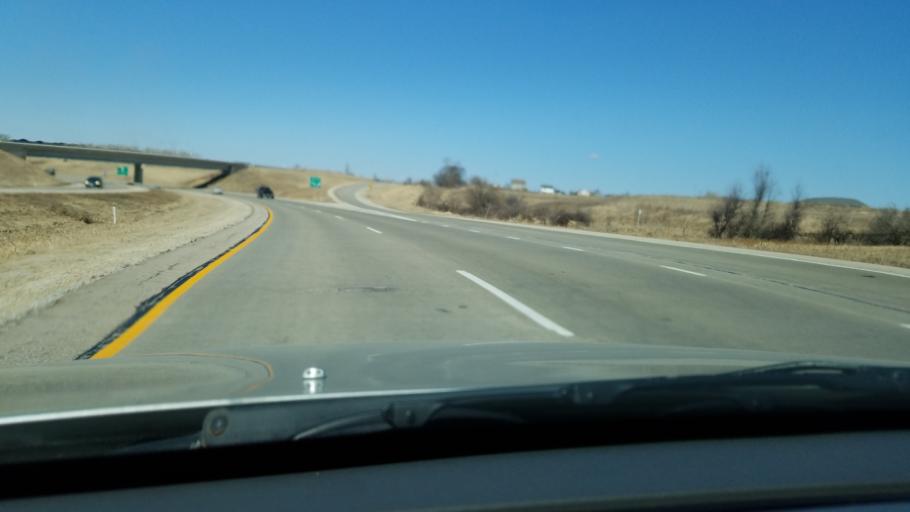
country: US
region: Wisconsin
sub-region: Dane County
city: Verona
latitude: 42.9829
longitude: -89.5574
